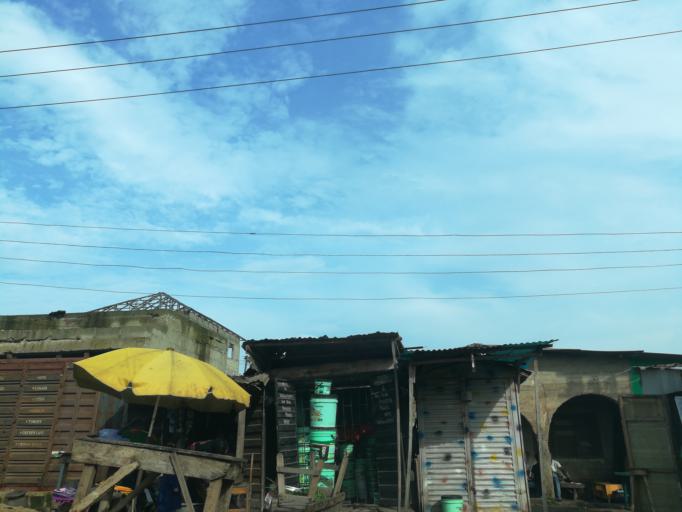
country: NG
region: Lagos
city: Ojota
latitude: 6.6063
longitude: 3.4220
